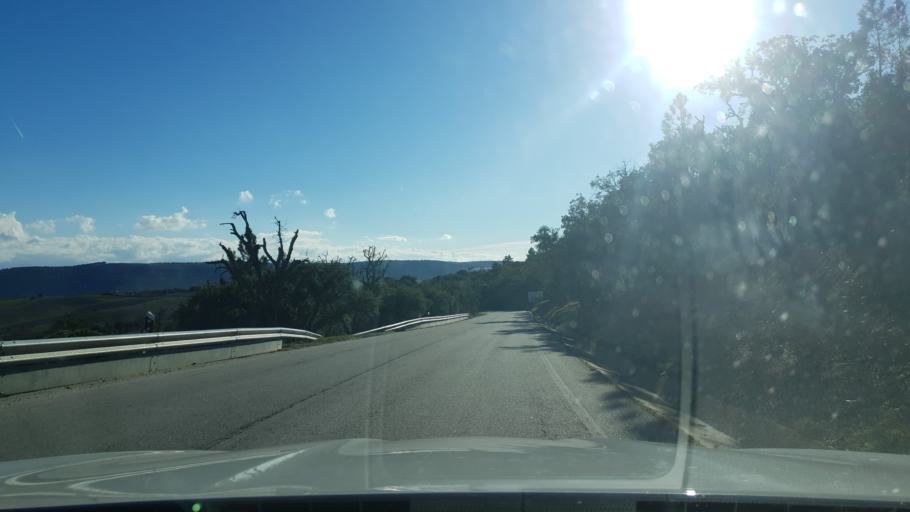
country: PT
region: Braganca
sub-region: Freixo de Espada A Cinta
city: Freixo de Espada a Cinta
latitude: 41.1002
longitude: -6.8302
